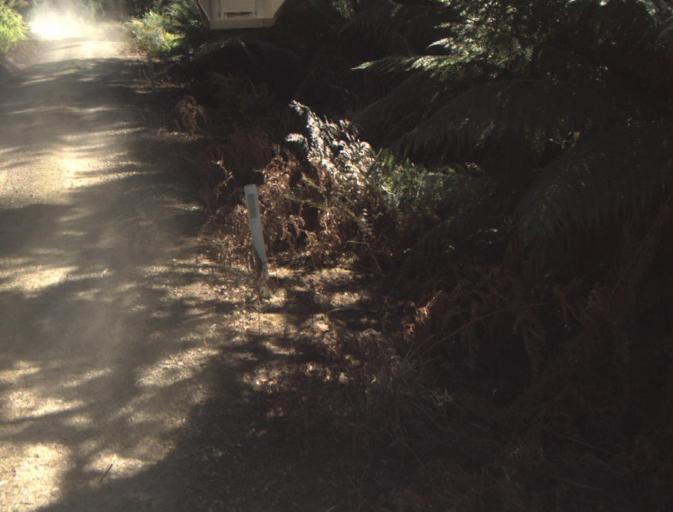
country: AU
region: Tasmania
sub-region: Dorset
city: Scottsdale
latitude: -41.2748
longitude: 147.3628
